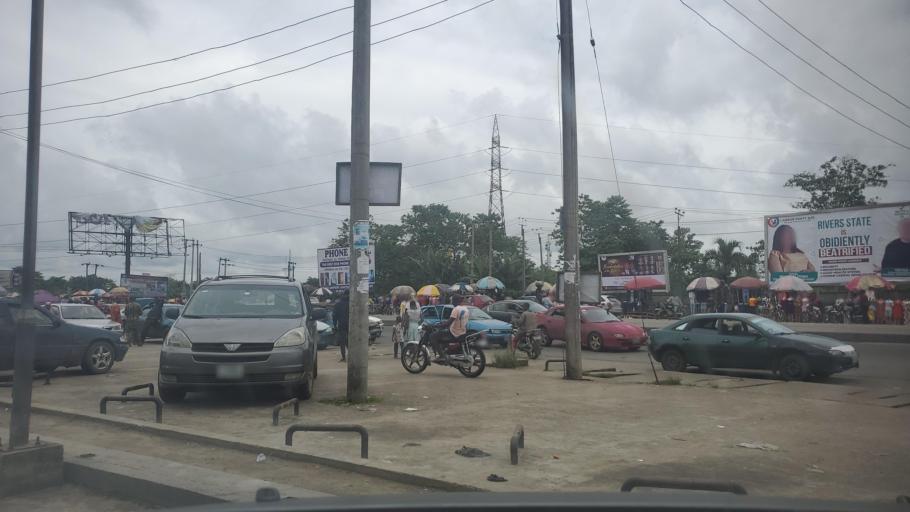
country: NG
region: Rivers
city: Emuoha
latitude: 4.8984
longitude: 6.9074
